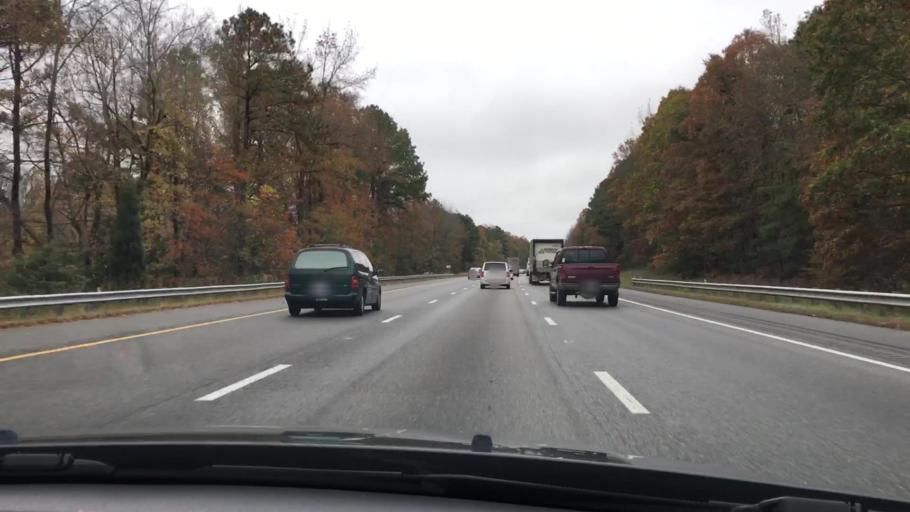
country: US
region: Virginia
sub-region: Caroline County
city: Bowling Green
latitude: 37.9646
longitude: -77.4885
